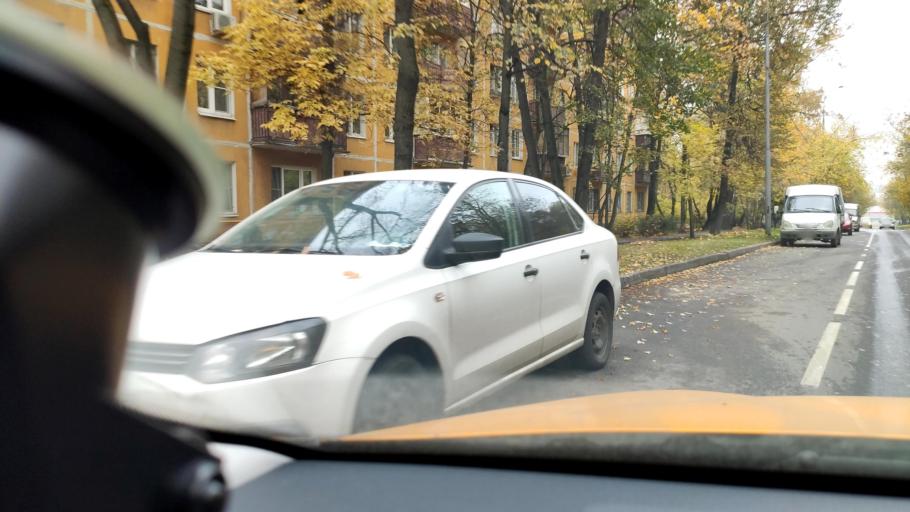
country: RU
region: Moskovskaya
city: Bol'shaya Setun'
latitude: 55.7235
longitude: 37.4365
